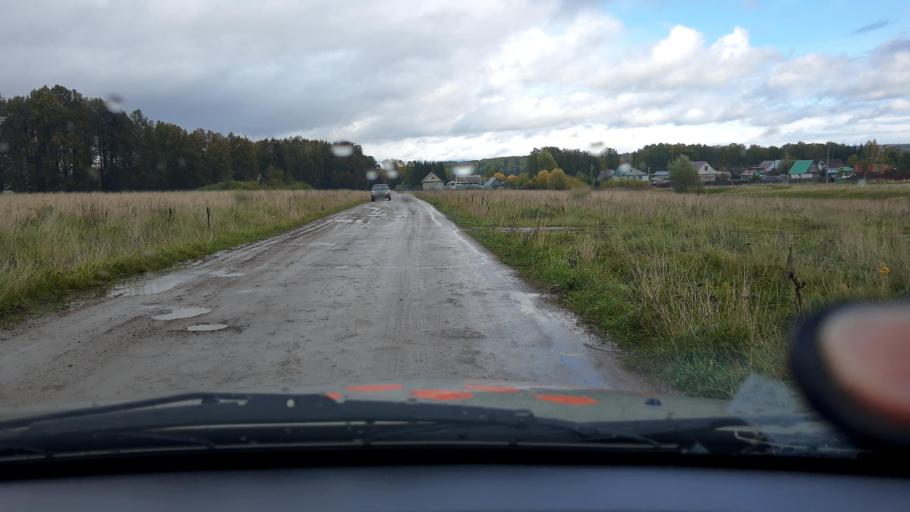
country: RU
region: Bashkortostan
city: Kudeyevskiy
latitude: 54.8776
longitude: 56.6292
